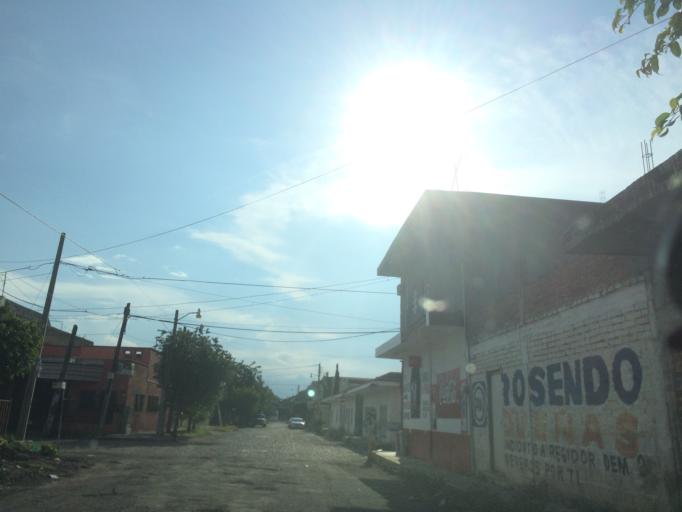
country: MX
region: Nayarit
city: Ixtlan del Rio
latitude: 21.0350
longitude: -104.3866
